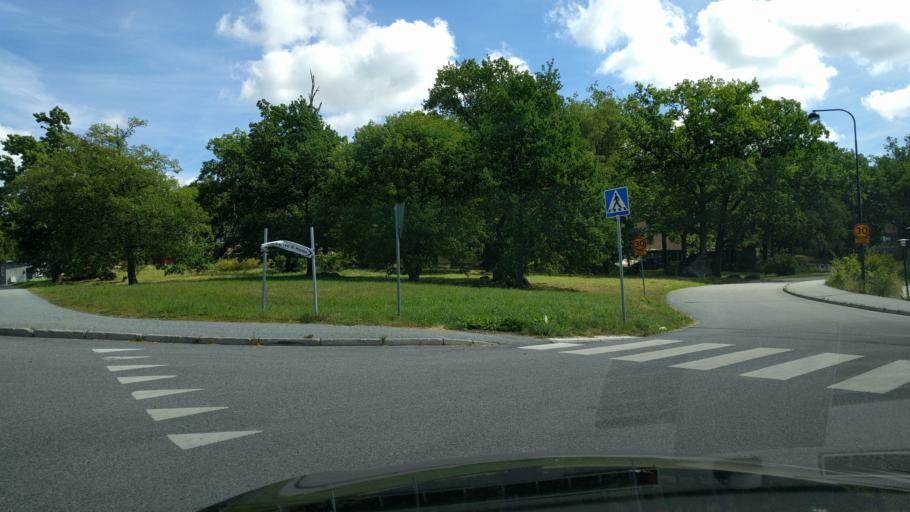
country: SE
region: Stockholm
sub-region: Jarfalla Kommun
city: Jakobsberg
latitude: 59.4193
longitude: 17.8585
